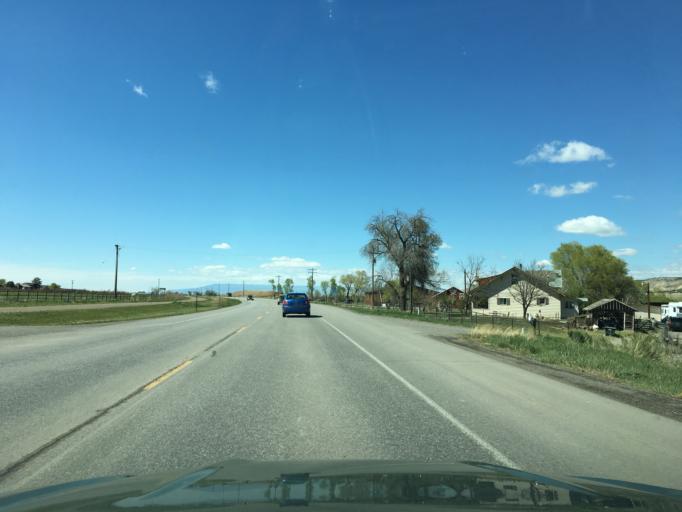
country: US
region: Colorado
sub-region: Montrose County
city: Montrose
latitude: 38.3428
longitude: -107.7888
